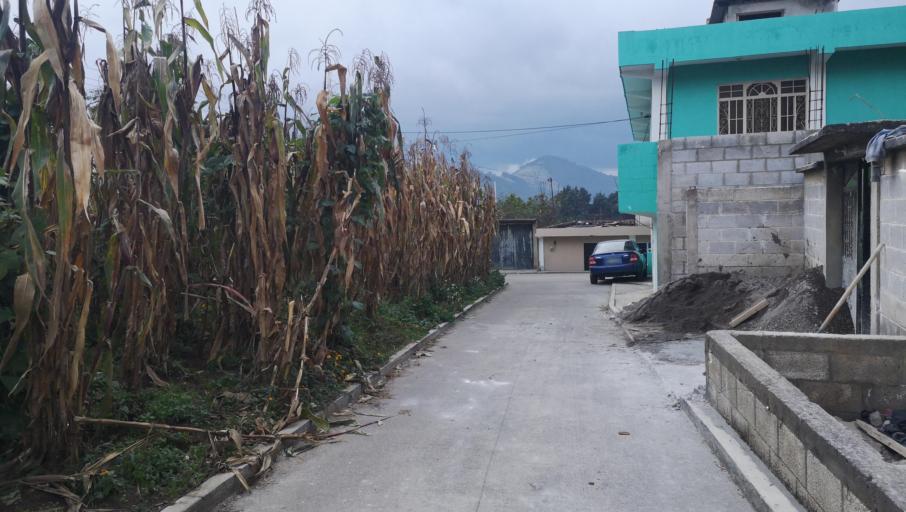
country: GT
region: Quetzaltenango
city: Cantel
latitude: 14.8195
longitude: -91.4359
